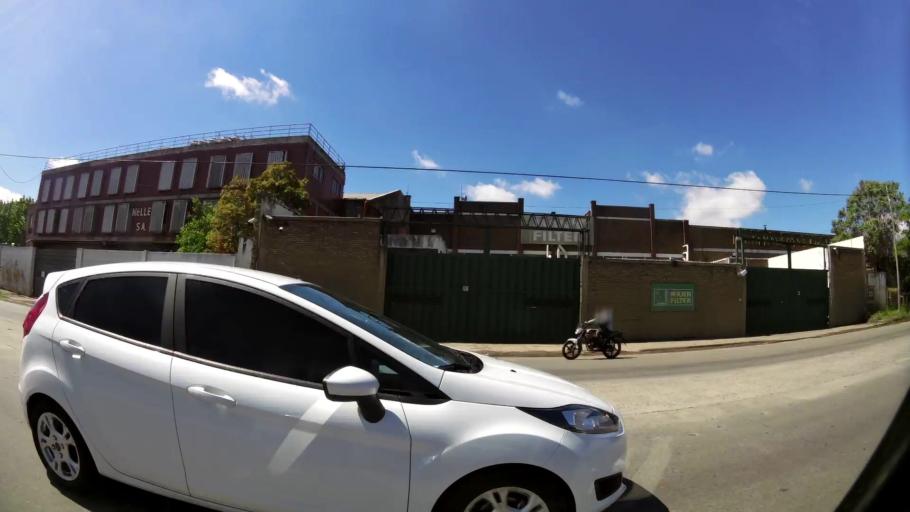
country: AR
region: Buenos Aires
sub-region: Partido de Lanus
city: Lanus
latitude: -34.6637
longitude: -58.4248
